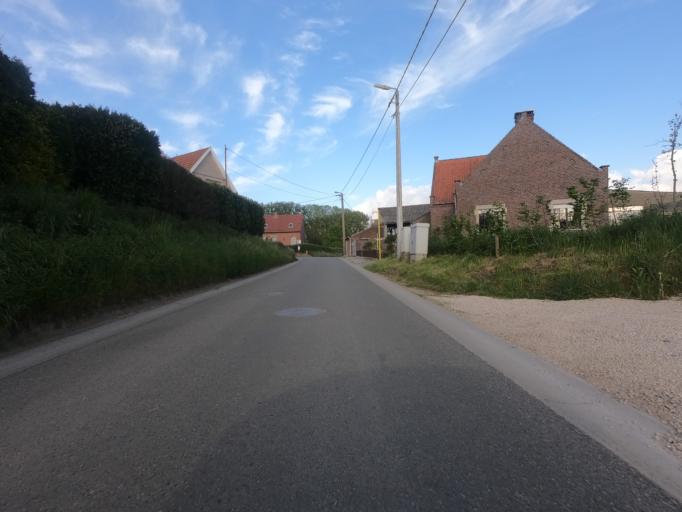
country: BE
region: Flanders
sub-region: Provincie Vlaams-Brabant
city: Galmaarden
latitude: 50.7524
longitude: 3.9994
